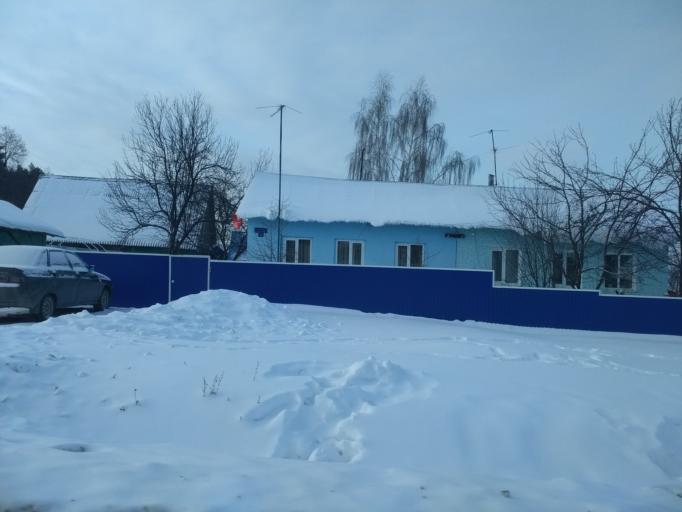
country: RU
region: Bashkortostan
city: Iglino
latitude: 54.7697
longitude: 56.5341
